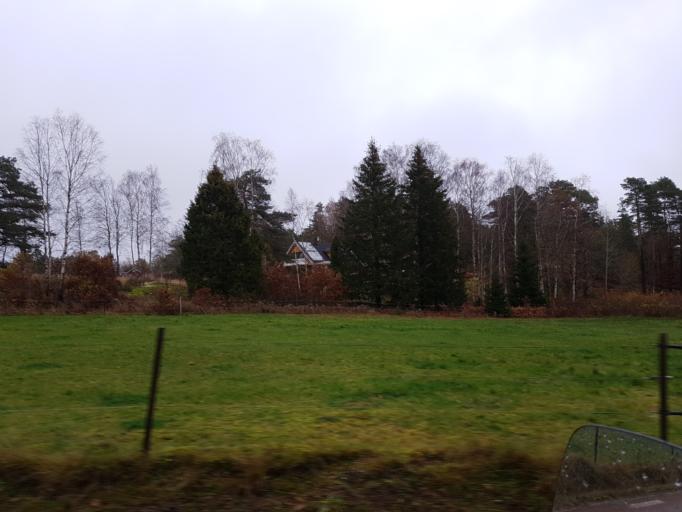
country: SE
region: Vaestra Goetaland
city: Svanesund
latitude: 58.1750
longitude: 11.8283
